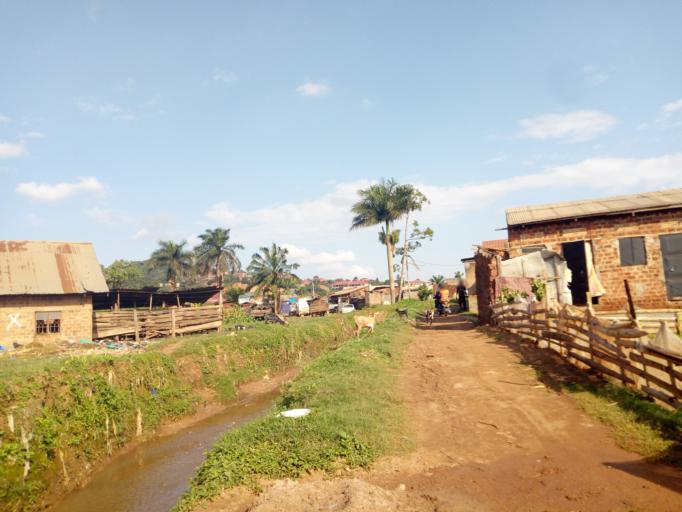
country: UG
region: Central Region
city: Kampala Central Division
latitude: 0.3464
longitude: 32.5567
